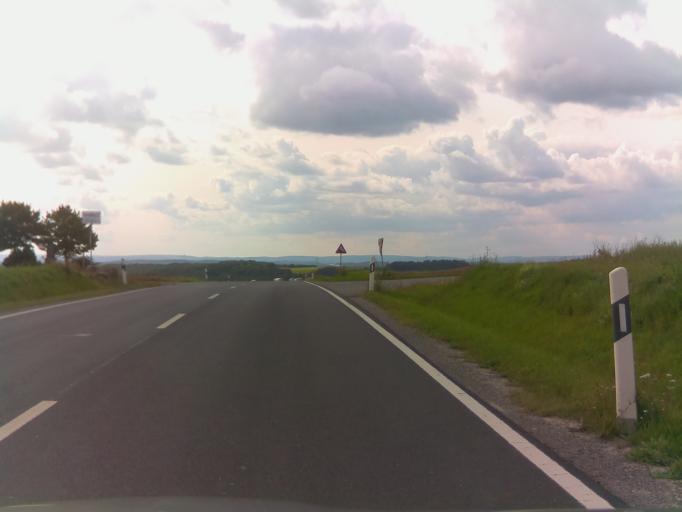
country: DE
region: Bavaria
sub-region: Regierungsbezirk Unterfranken
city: Retzstadt
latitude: 49.9156
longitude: 9.9021
